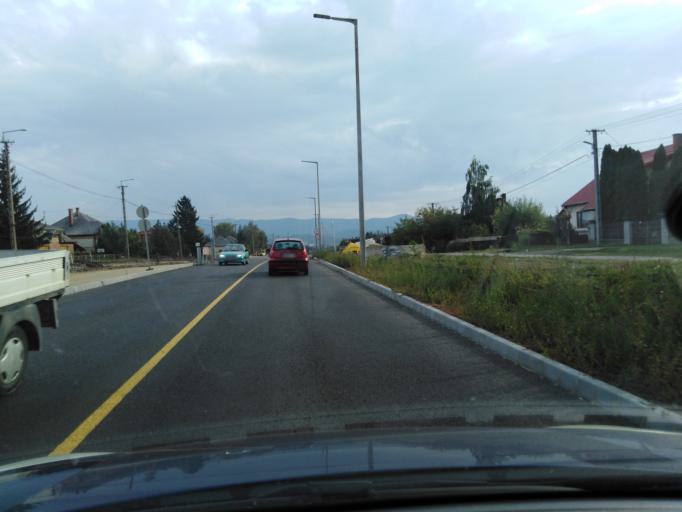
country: HU
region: Nograd
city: Kazar
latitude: 48.0186
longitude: 19.8210
